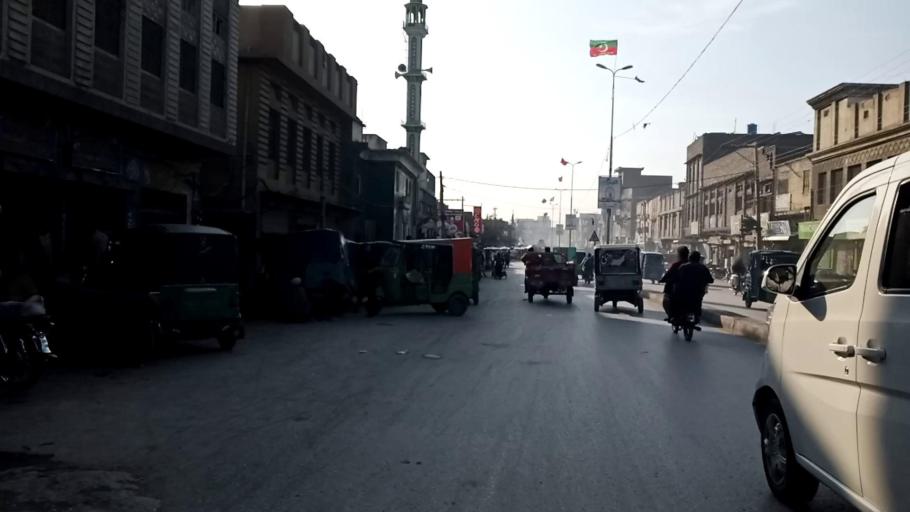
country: PK
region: Khyber Pakhtunkhwa
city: Peshawar
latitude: 34.0047
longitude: 71.5760
